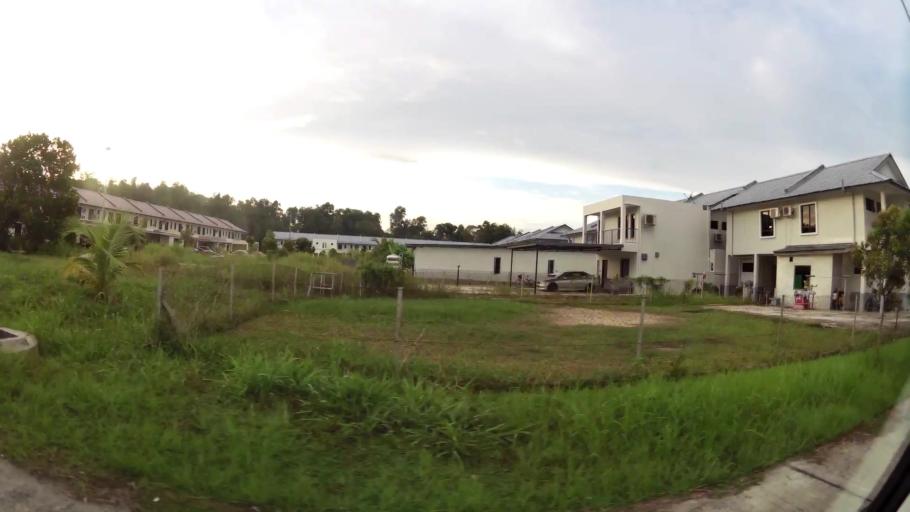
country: BN
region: Brunei and Muara
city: Bandar Seri Begawan
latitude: 4.9955
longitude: 114.9874
